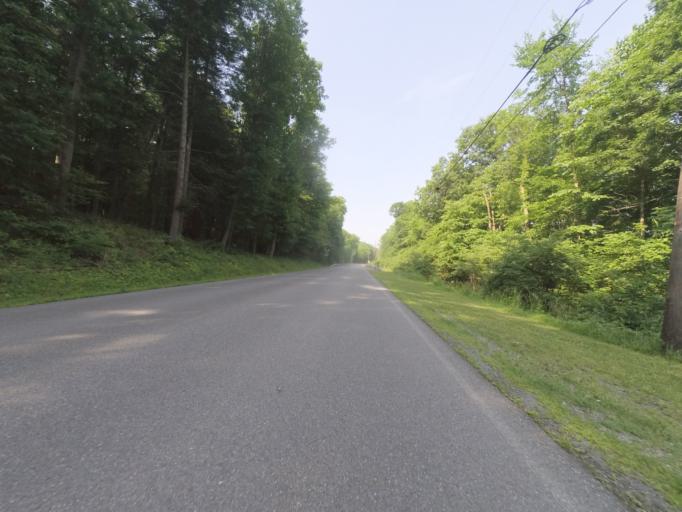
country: US
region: Pennsylvania
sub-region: Centre County
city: Zion
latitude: 40.9753
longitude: -77.7151
